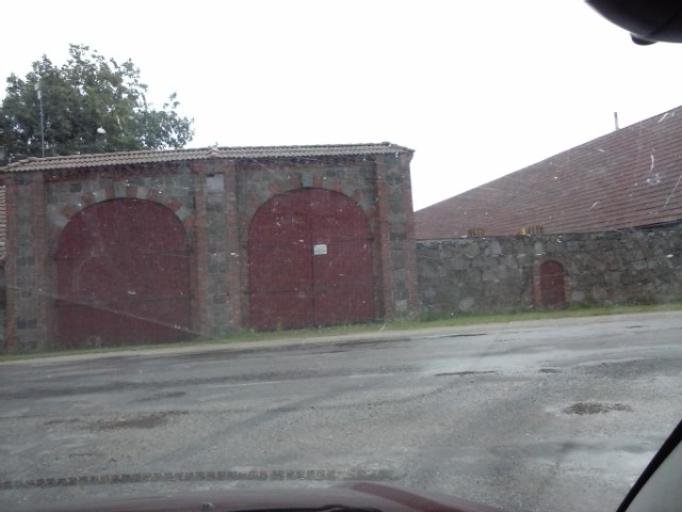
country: EE
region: Tartu
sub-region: Tartu linn
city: Tartu
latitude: 58.3571
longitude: 26.8793
